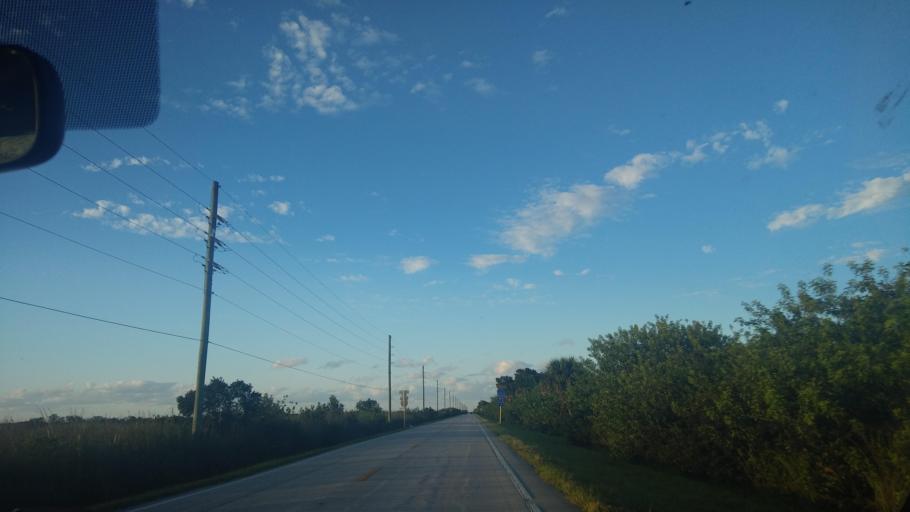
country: US
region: Florida
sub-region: Indian River County
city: Fellsmere
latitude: 27.6833
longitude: -80.6430
